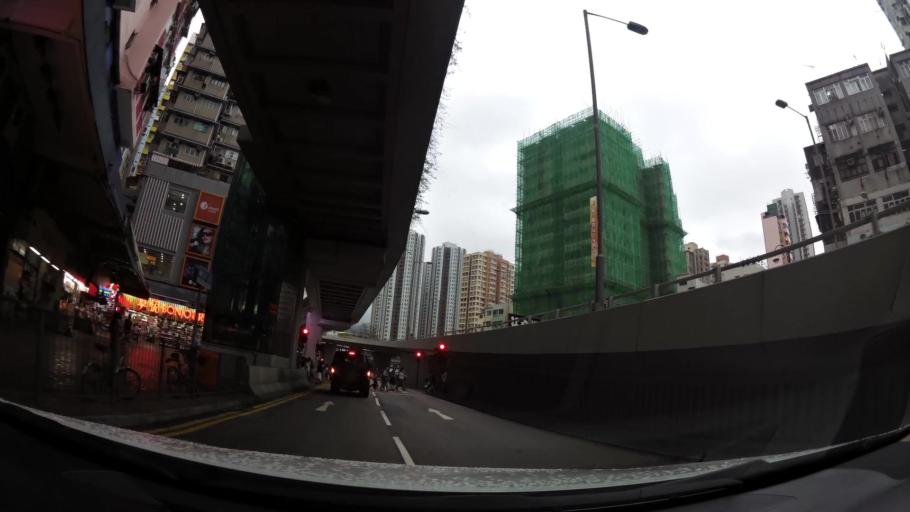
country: HK
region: Tsuen Wan
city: Tsuen Wan
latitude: 22.3722
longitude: 114.1160
